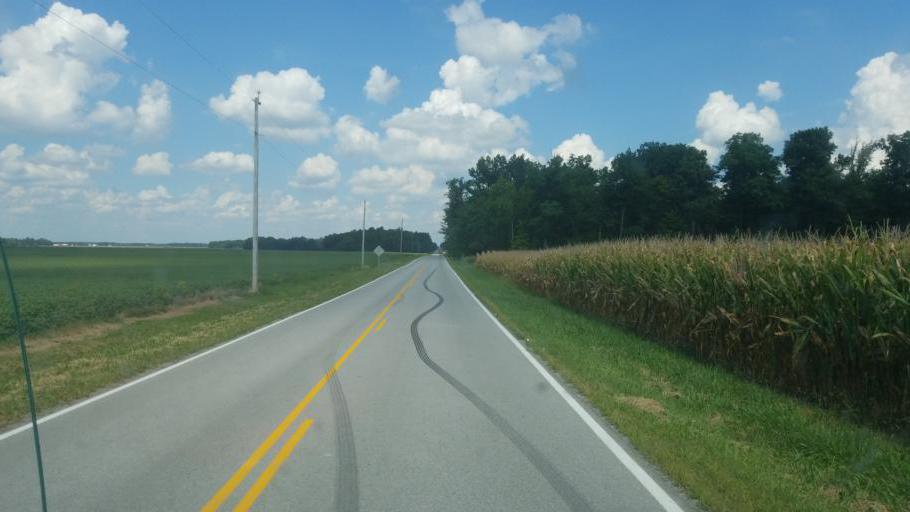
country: US
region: Ohio
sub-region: Hancock County
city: Arlington
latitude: 40.8346
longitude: -83.7278
